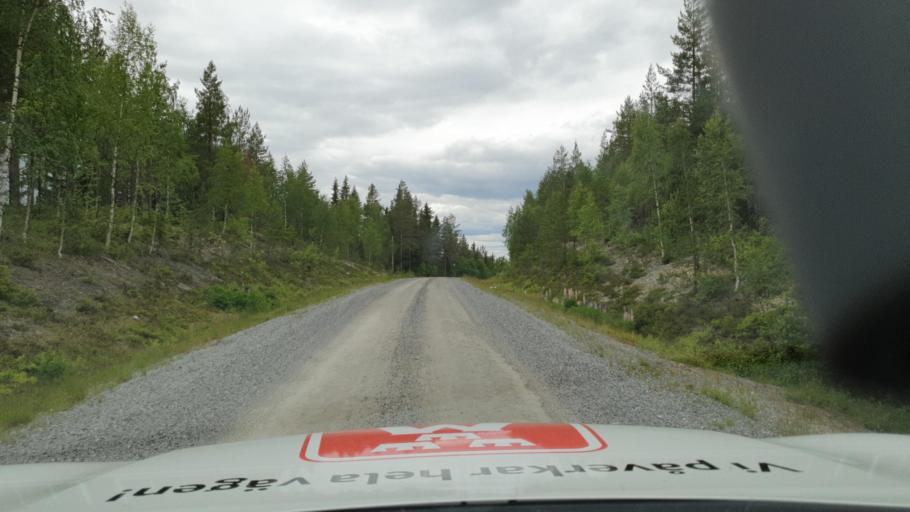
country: SE
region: Vaesterbotten
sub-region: Bjurholms Kommun
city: Bjurholm
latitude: 63.7639
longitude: 19.3444
